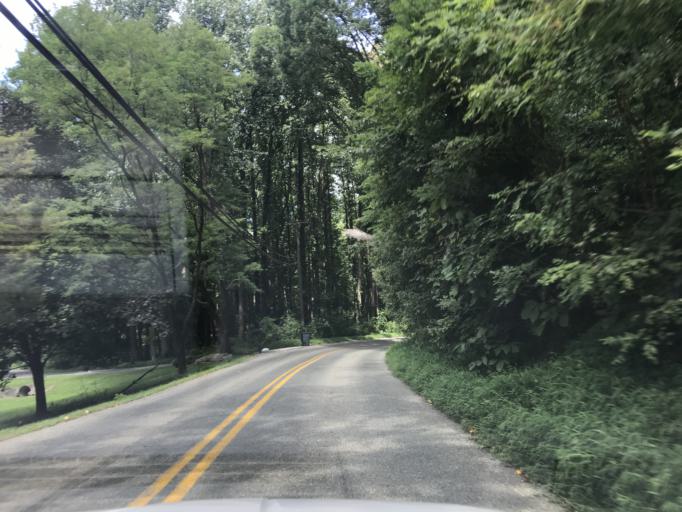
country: US
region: Maryland
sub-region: Harford County
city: Fallston
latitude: 39.5312
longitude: -76.4308
